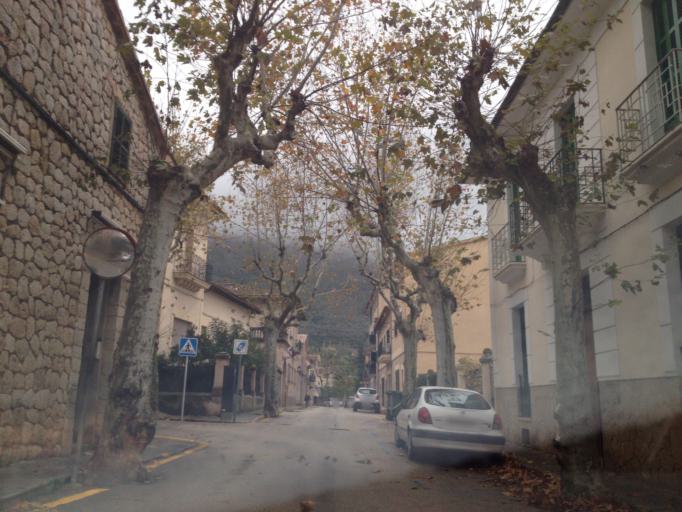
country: ES
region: Balearic Islands
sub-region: Illes Balears
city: Soller
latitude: 39.7692
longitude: 2.7110
